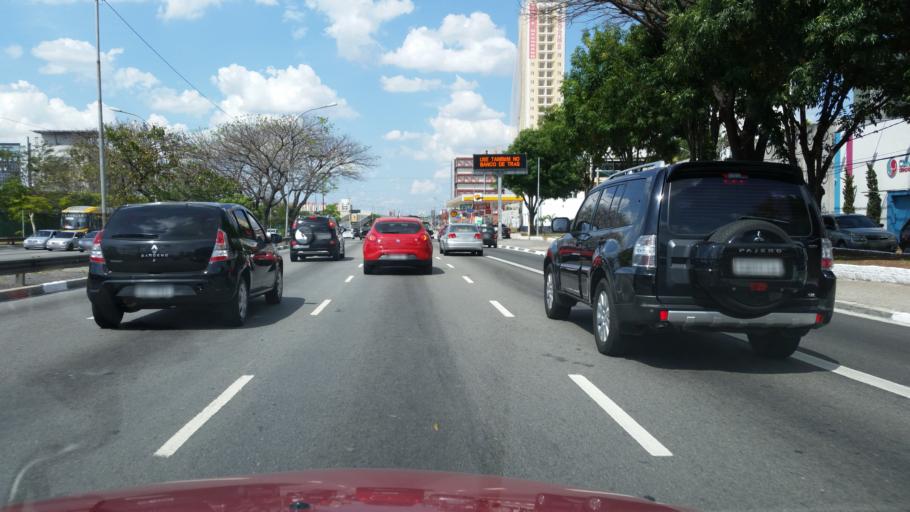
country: BR
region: Sao Paulo
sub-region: Sao Paulo
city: Sao Paulo
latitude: -23.5379
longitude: -46.5618
